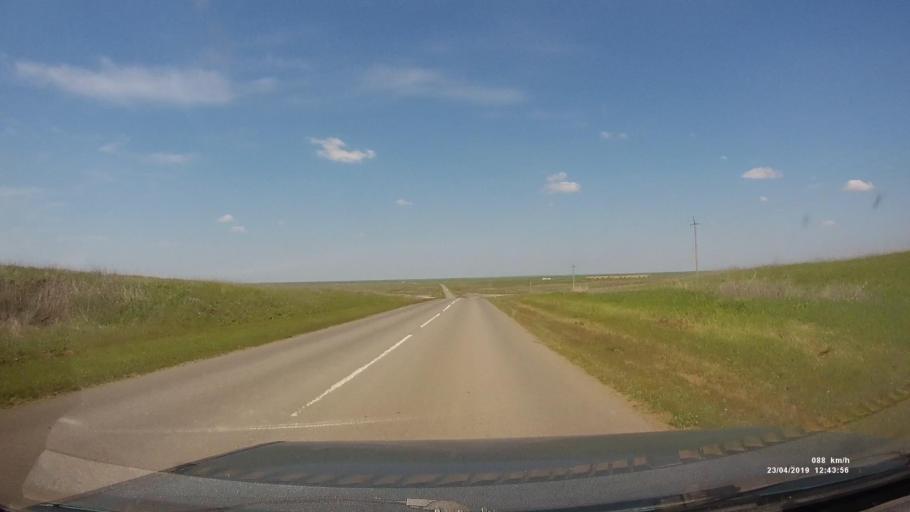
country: RU
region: Kalmykiya
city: Yashalta
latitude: 46.4705
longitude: 42.6498
